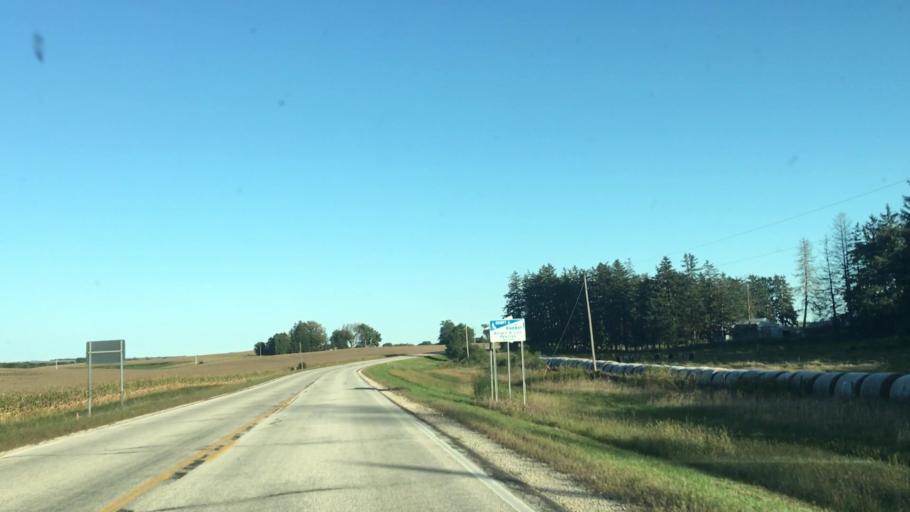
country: US
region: Minnesota
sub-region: Fillmore County
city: Chatfield
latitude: 43.8395
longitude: -92.0781
